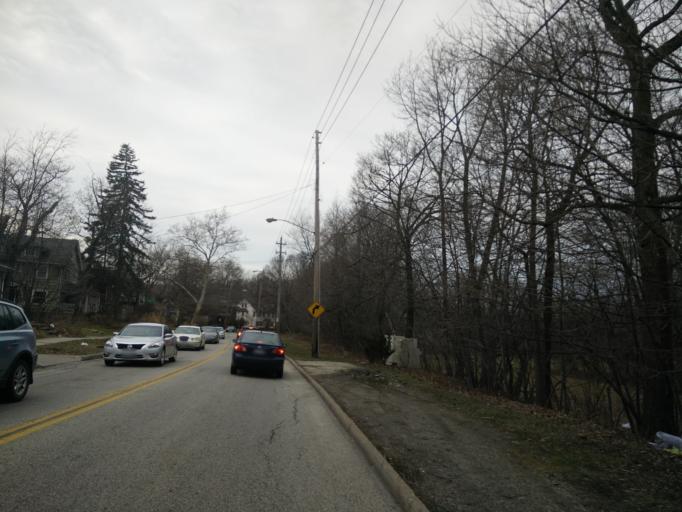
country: US
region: Ohio
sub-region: Cuyahoga County
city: Cleveland Heights
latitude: 41.5084
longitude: -81.5660
